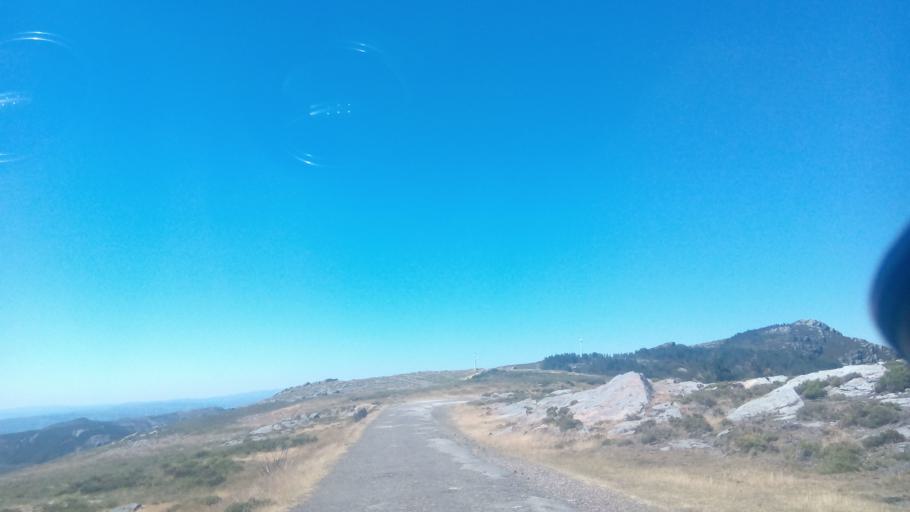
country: PT
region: Vila Real
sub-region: Mesao Frio
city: Mesao Frio
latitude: 41.2505
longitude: -7.8968
